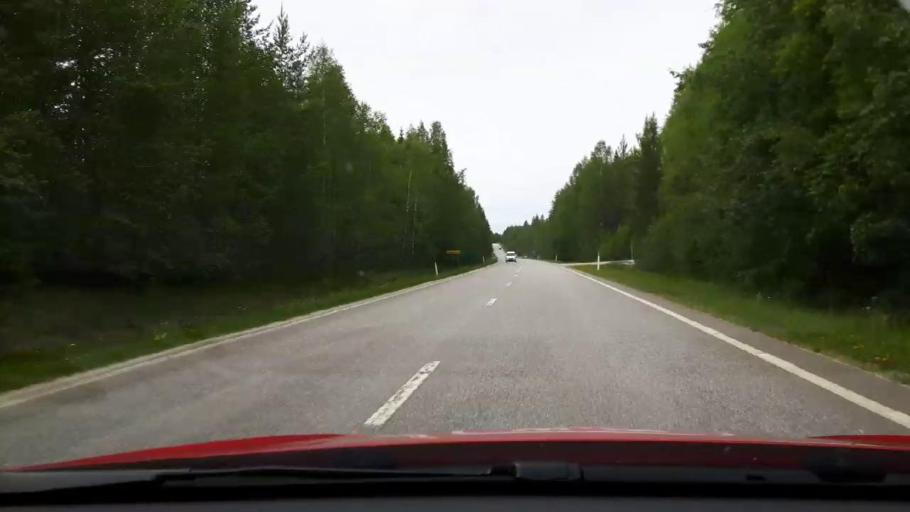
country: SE
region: Jaemtland
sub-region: Harjedalens Kommun
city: Sveg
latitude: 62.0977
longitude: 14.2283
